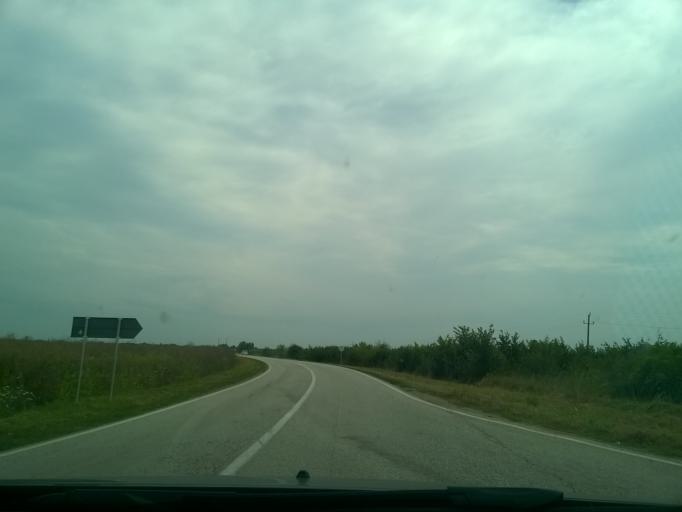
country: RS
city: Banatski Despotovac
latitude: 45.3779
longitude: 20.6763
